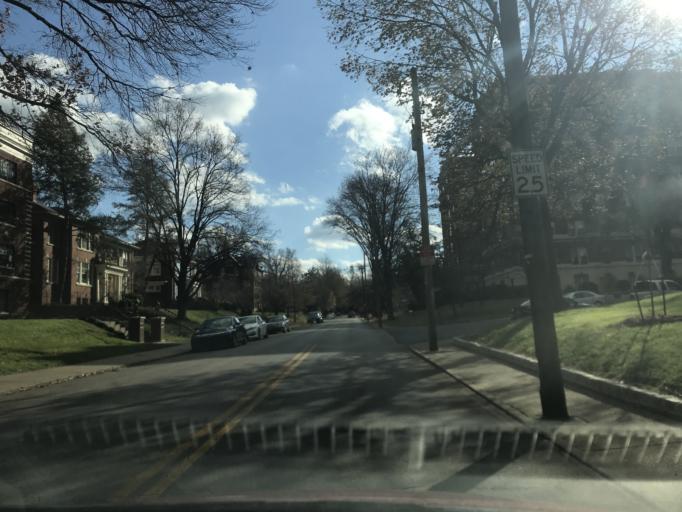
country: US
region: Kentucky
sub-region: Jefferson County
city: Audubon Park
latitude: 38.2355
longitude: -85.7086
